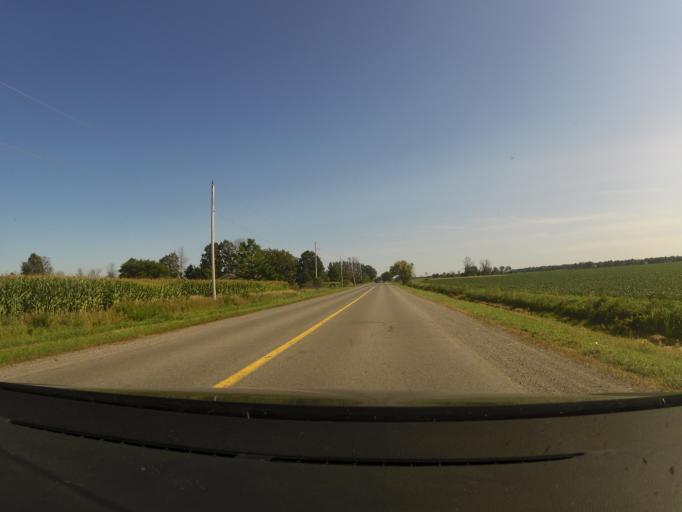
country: CA
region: Ontario
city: Carleton Place
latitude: 45.3452
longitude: -76.0826
